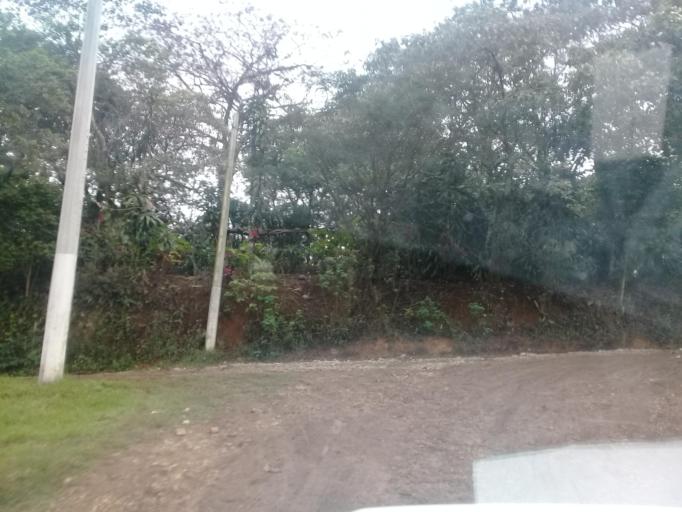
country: MX
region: Veracruz
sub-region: Cordoba
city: San Jose de Tapia
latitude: 18.8557
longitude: -96.9606
